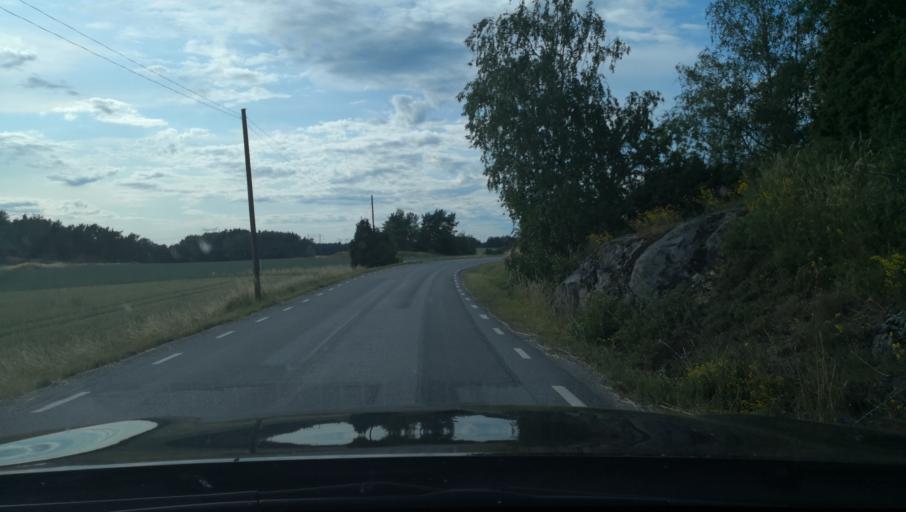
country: SE
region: Uppsala
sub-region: Habo Kommun
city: Balsta
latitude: 59.6685
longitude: 17.4425
